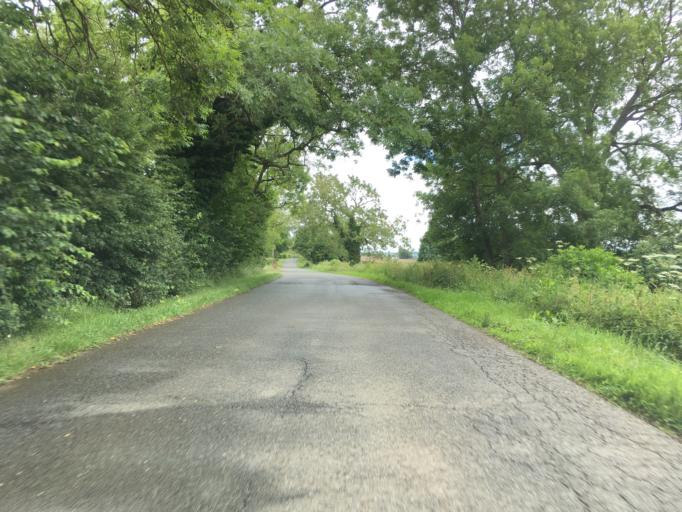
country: GB
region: England
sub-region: Northamptonshire
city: Daventry
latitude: 52.2433
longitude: -1.1978
